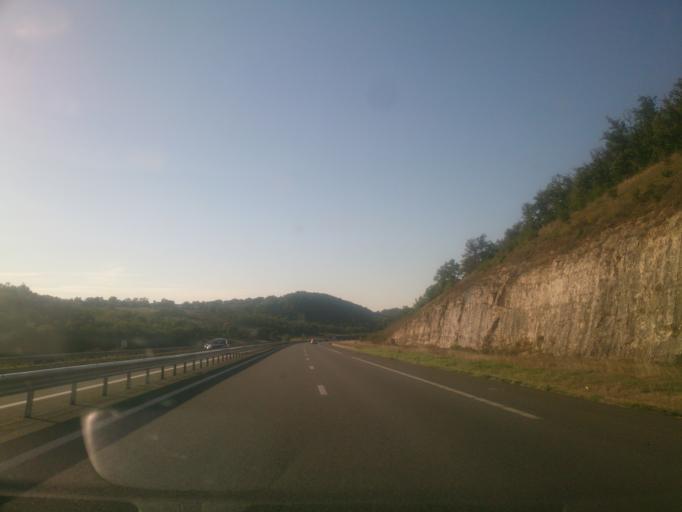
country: FR
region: Midi-Pyrenees
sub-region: Departement du Lot
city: Le Vigan
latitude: 44.7446
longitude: 1.5485
